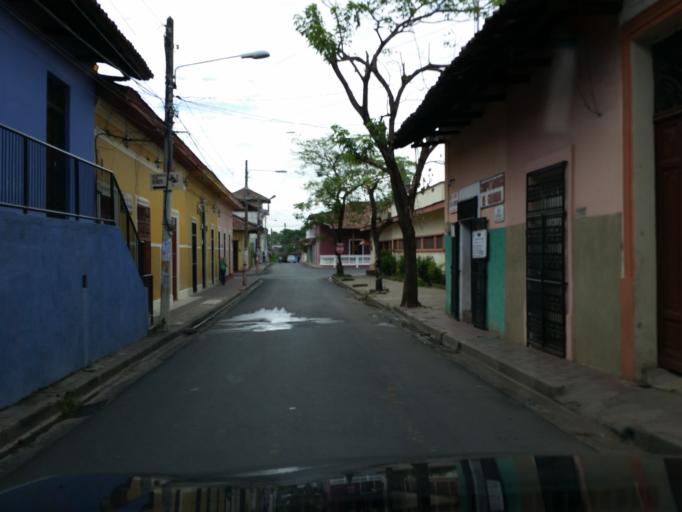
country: NI
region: Granada
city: Granada
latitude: 11.9315
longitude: -85.9567
